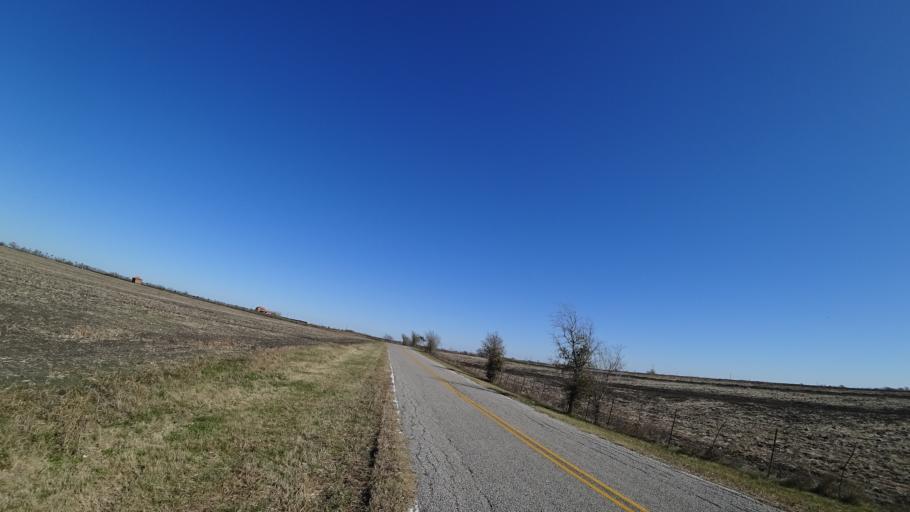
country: US
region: Texas
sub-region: Travis County
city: Garfield
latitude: 30.0977
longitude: -97.6388
